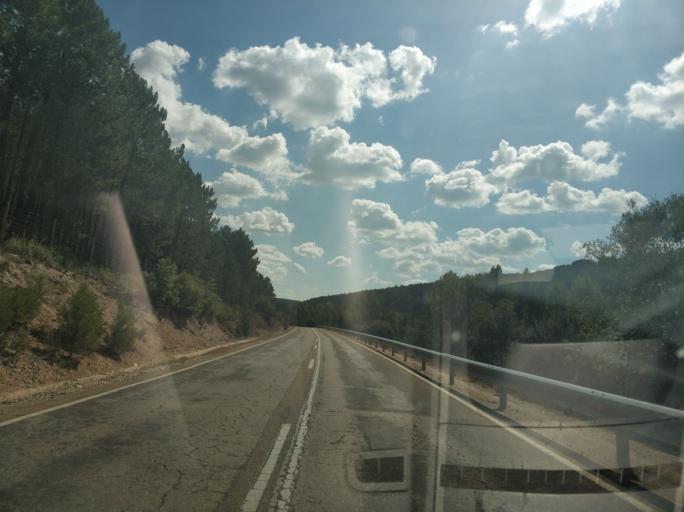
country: ES
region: Castille and Leon
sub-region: Provincia de Soria
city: Casarejos
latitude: 41.8008
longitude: -3.0412
